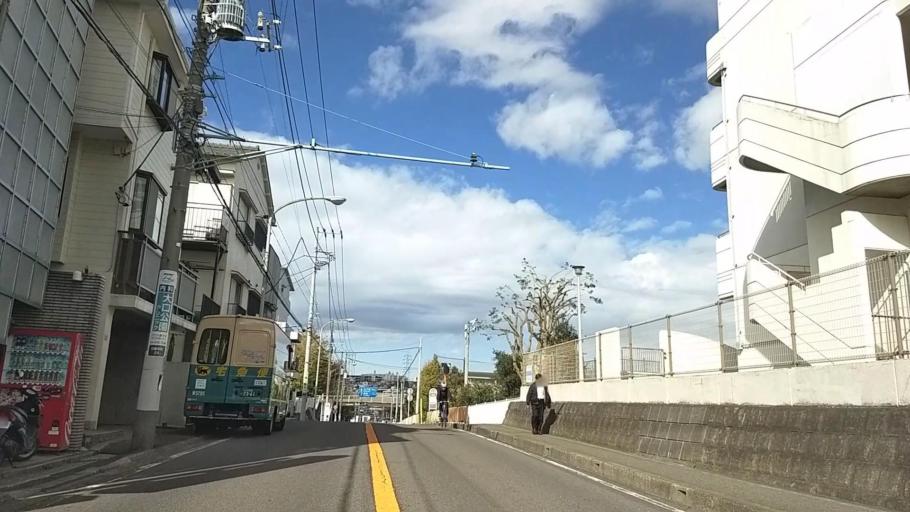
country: JP
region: Kanagawa
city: Yokohama
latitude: 35.4856
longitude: 139.6405
